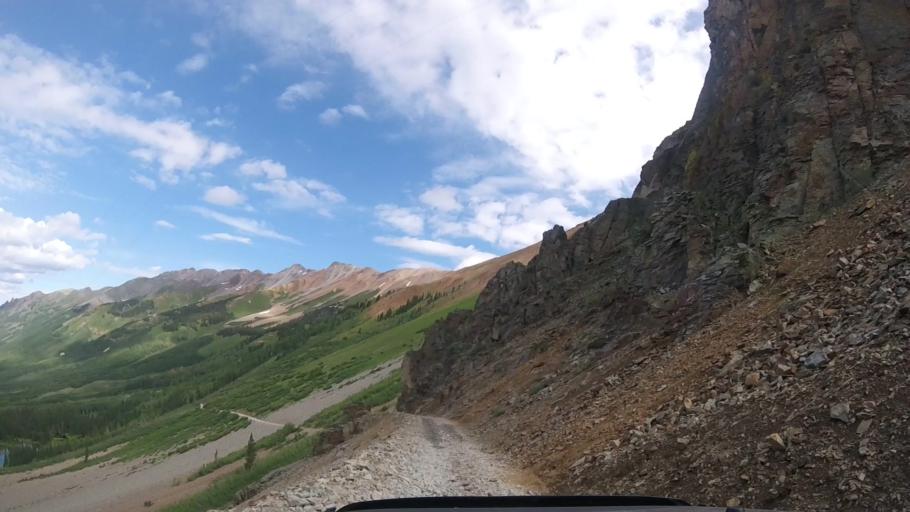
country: US
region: Colorado
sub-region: San Miguel County
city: Telluride
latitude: 37.8552
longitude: -107.7868
